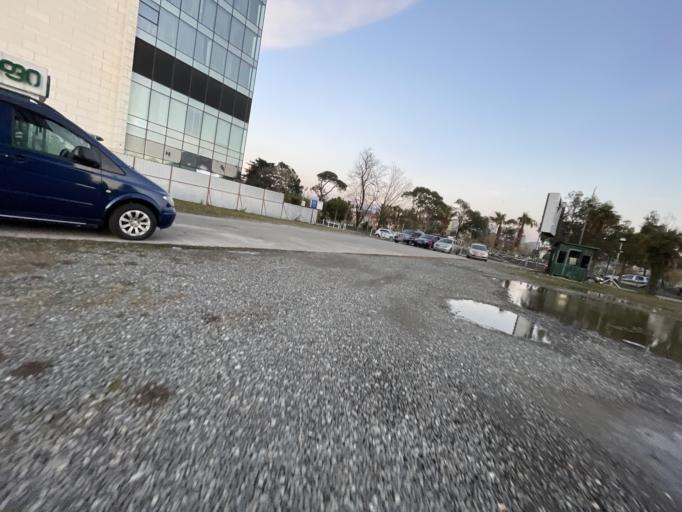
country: GE
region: Ajaria
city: Batumi
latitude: 41.6489
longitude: 41.6249
